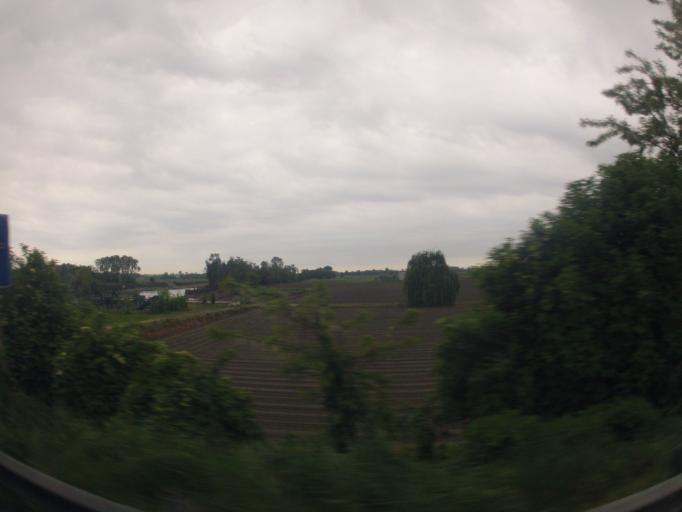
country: IT
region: Piedmont
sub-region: Provincia di Cuneo
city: Casalgrasso
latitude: 44.8256
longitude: 7.6245
